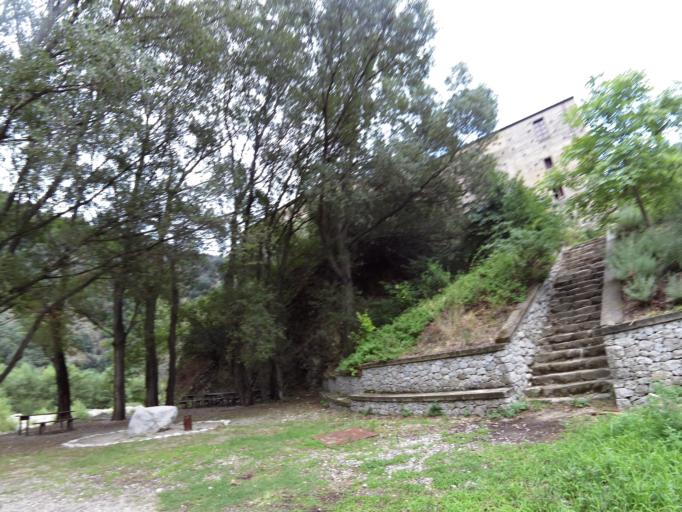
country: IT
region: Calabria
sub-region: Provincia di Reggio Calabria
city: Caulonia
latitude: 38.4247
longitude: 16.3771
